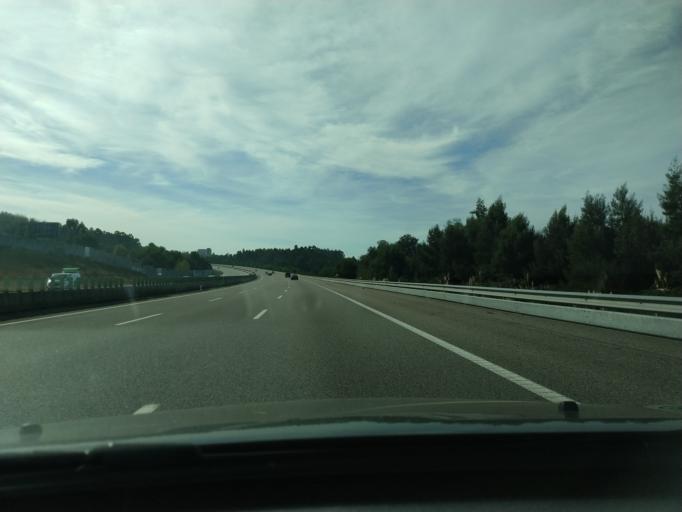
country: PT
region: Aveiro
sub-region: Santa Maria da Feira
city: Feira
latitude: 40.8939
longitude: -8.5686
